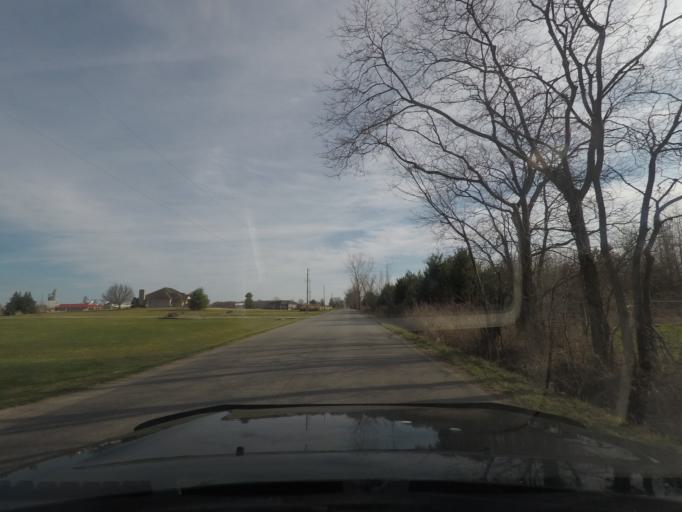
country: US
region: Indiana
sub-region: Elkhart County
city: Dunlap
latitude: 41.5566
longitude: -85.9249
